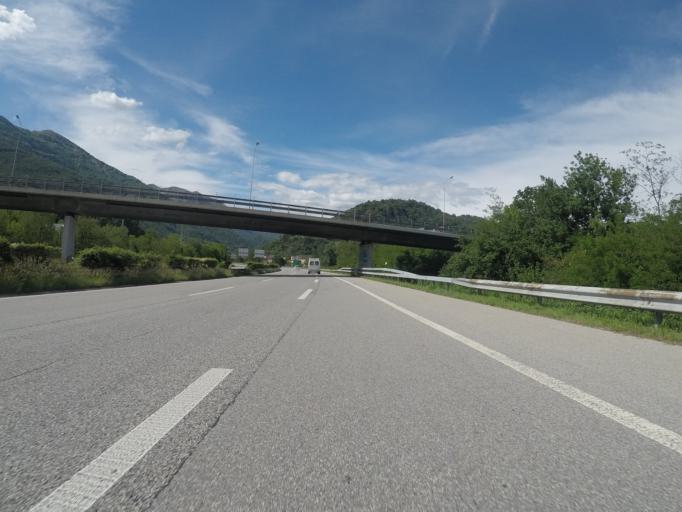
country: CH
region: Ticino
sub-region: Lugano District
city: Cadempino
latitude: 46.0378
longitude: 8.9294
